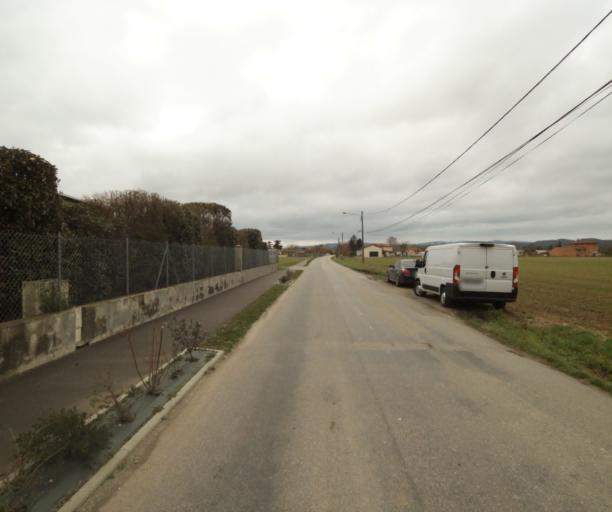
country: FR
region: Midi-Pyrenees
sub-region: Departement de l'Ariege
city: La Tour-du-Crieu
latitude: 43.1528
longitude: 1.6365
